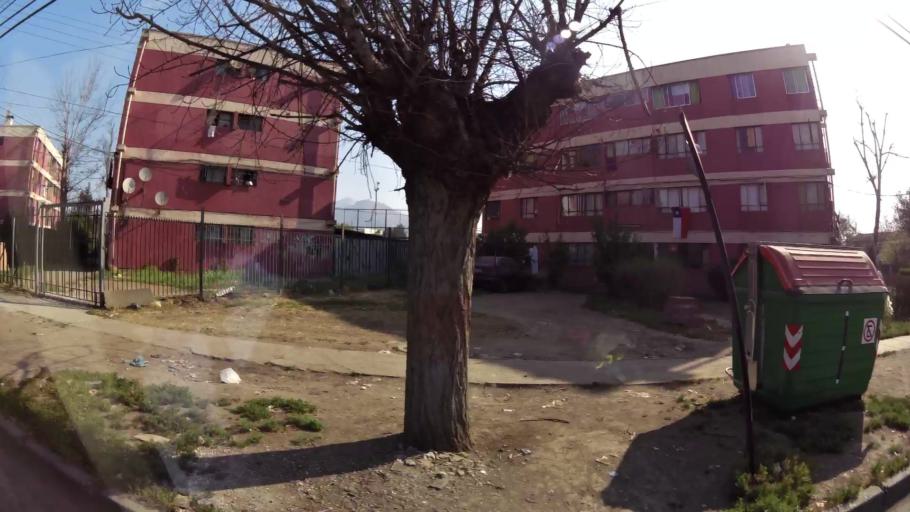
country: CL
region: Santiago Metropolitan
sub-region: Provincia de Santiago
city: Lo Prado
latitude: -33.3716
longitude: -70.6857
